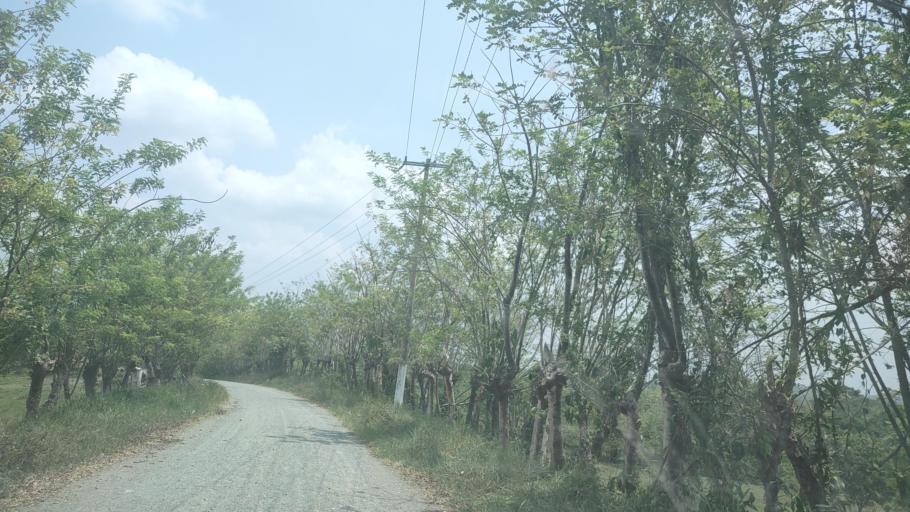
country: MX
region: Tabasco
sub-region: Huimanguillo
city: Francisco Rueda
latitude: 17.5826
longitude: -93.9591
